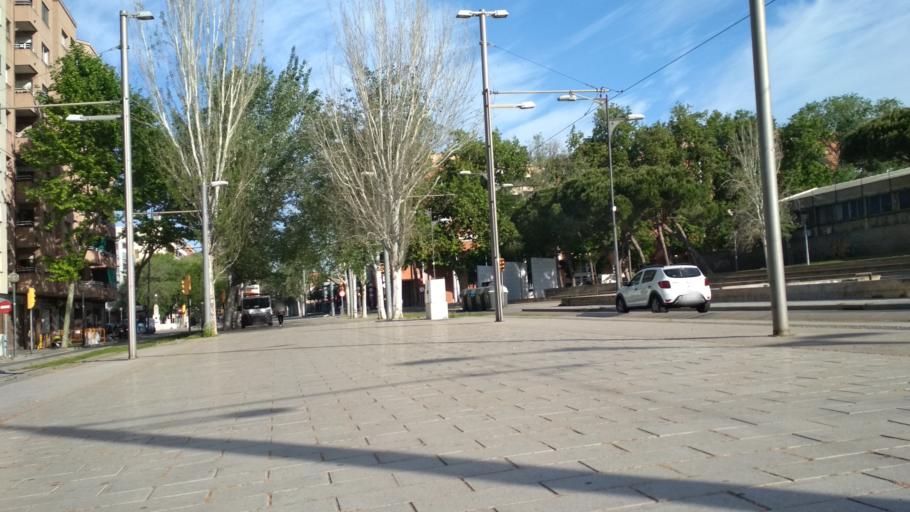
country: ES
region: Catalonia
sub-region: Provincia de Barcelona
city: Sant Adria de Besos
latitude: 41.4275
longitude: 2.2252
